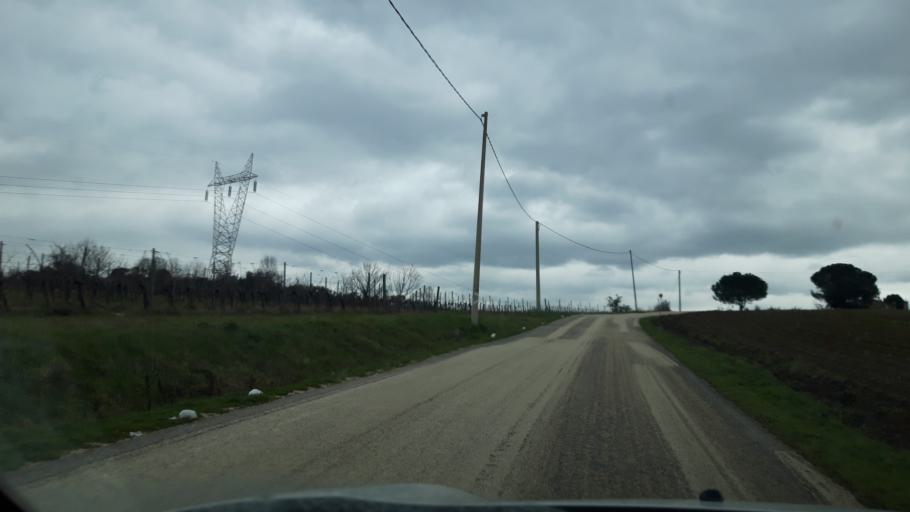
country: IT
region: Umbria
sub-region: Provincia di Perugia
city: Tavernelle
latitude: 42.9902
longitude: 12.1722
